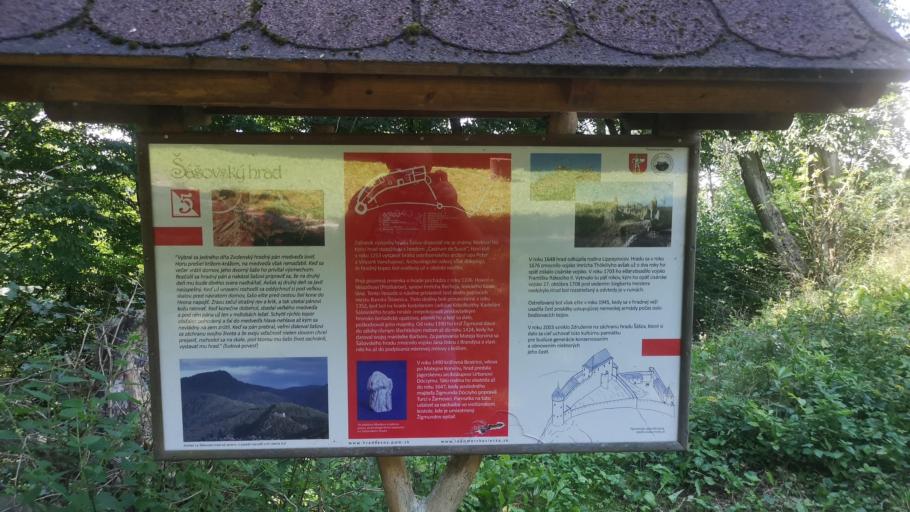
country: SK
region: Banskobystricky
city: Ziar nad Hronom
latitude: 48.5786
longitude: 18.9006
